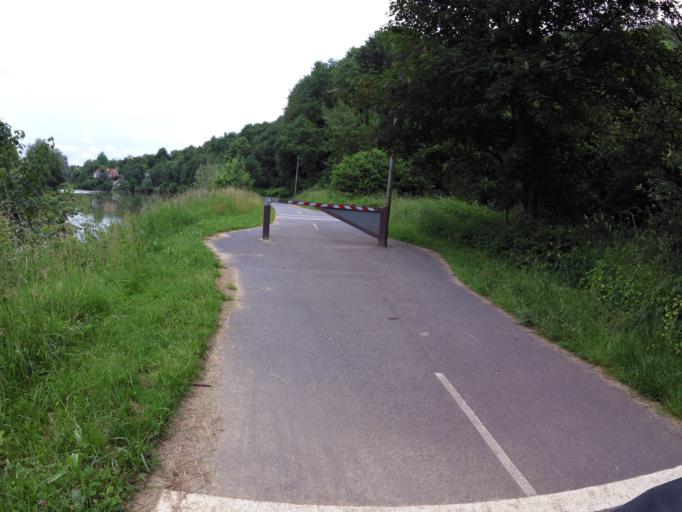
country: FR
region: Champagne-Ardenne
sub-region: Departement des Ardennes
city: Montcy-Notre-Dame
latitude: 49.7683
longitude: 4.7323
